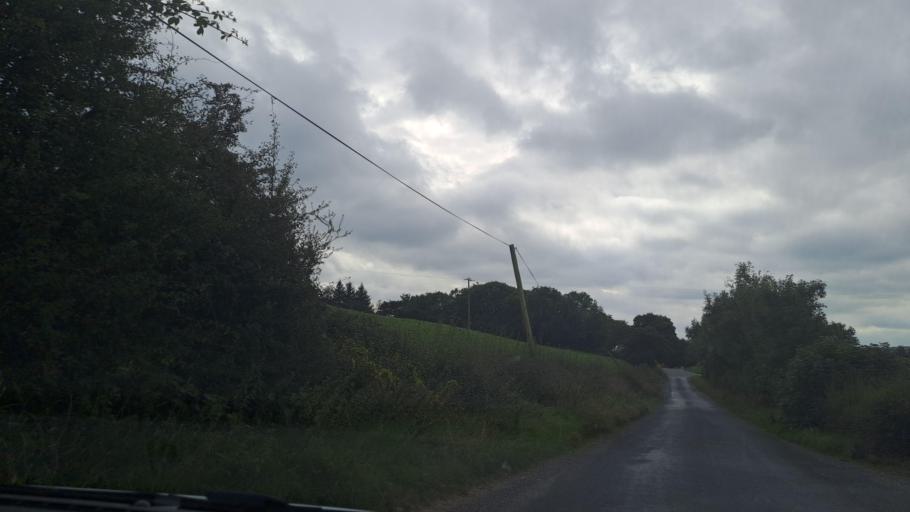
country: IE
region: Ulster
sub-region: An Cabhan
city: Bailieborough
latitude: 53.9424
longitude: -6.9083
